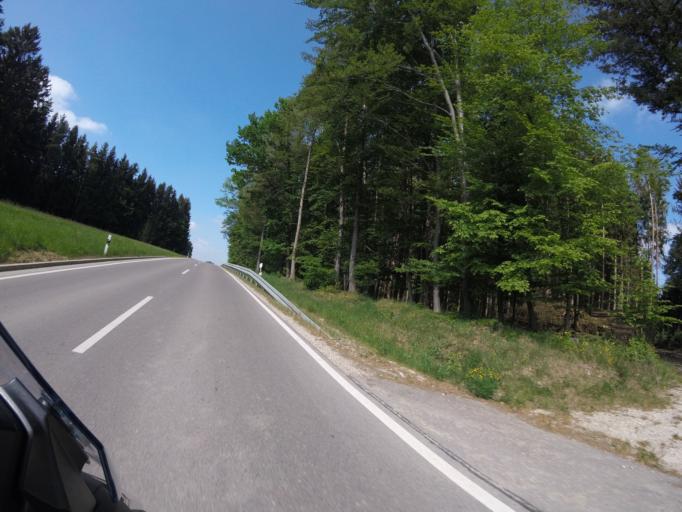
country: DE
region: Bavaria
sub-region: Upper Bavaria
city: Jetzendorf
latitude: 48.4495
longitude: 11.4184
